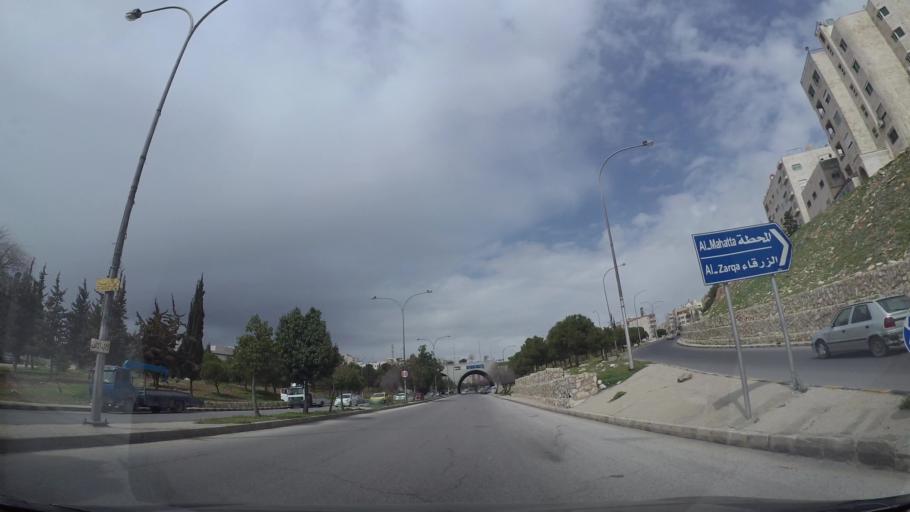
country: JO
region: Amman
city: Amman
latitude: 31.9780
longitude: 35.9188
